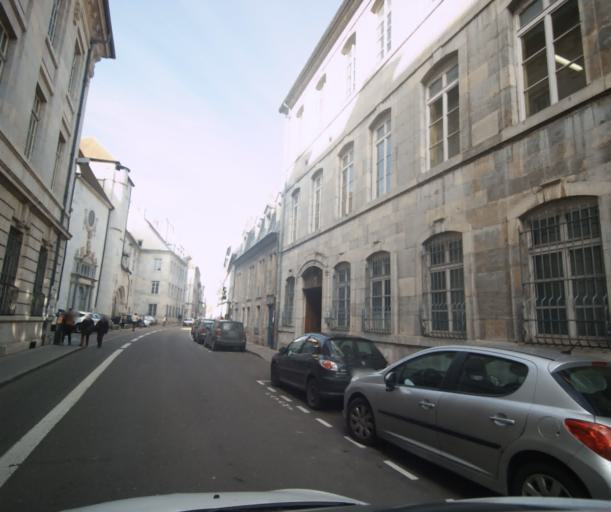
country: FR
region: Franche-Comte
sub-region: Departement du Doubs
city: Besancon
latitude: 47.2344
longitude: 6.0256
